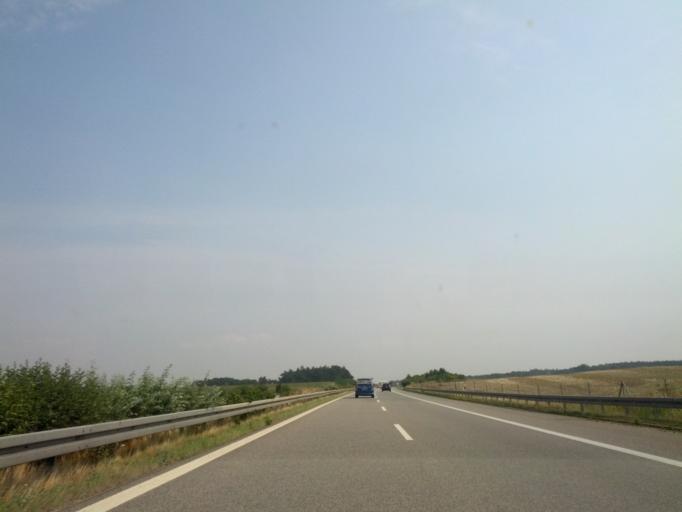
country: DE
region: Mecklenburg-Vorpommern
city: Tessin
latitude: 54.0105
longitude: 12.4920
